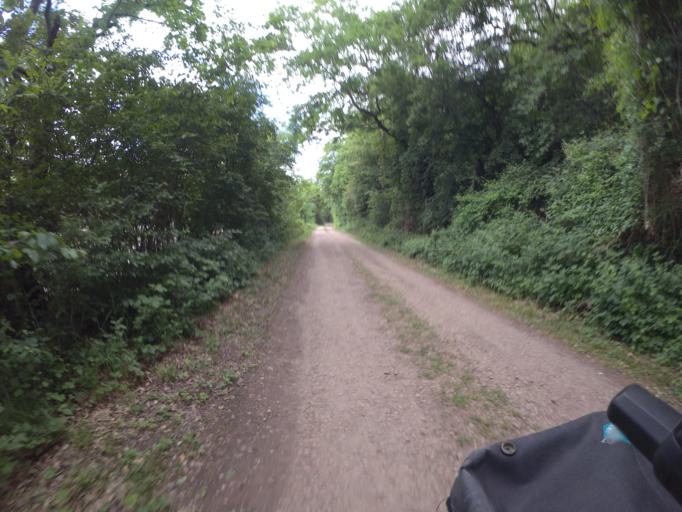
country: DE
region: Rheinland-Pfalz
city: Niederhausen
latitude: 49.8056
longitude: 7.7878
